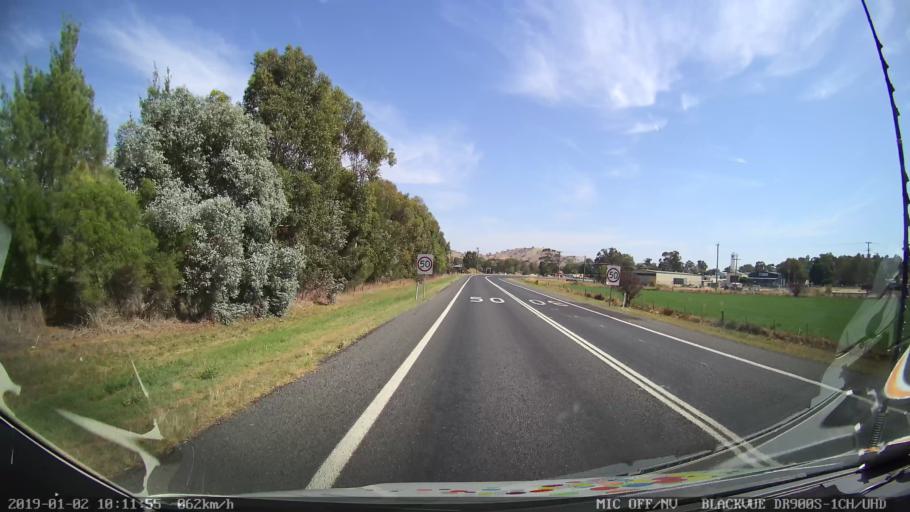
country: AU
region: New South Wales
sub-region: Gundagai
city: Gundagai
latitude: -35.0886
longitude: 148.0937
